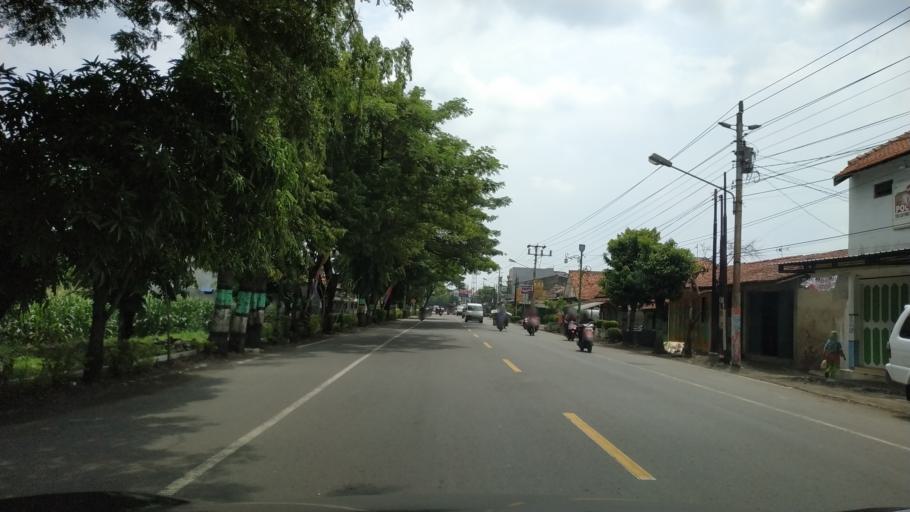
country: ID
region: Central Java
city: Slawi
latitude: -6.9941
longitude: 109.1416
